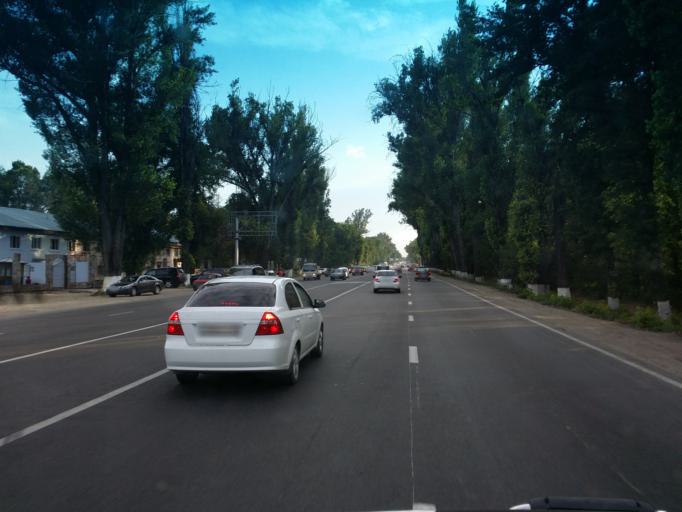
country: KZ
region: Almaty Qalasy
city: Almaty
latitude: 43.3044
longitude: 77.0107
